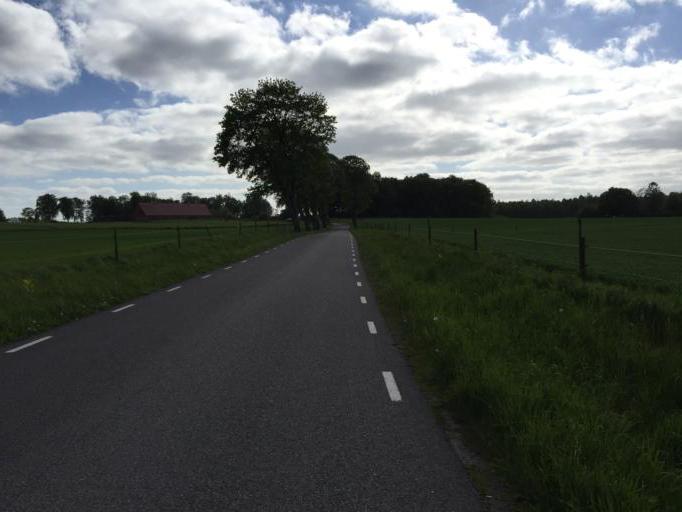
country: SE
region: Skane
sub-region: Sjobo Kommun
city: Blentarp
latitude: 55.6524
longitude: 13.6037
